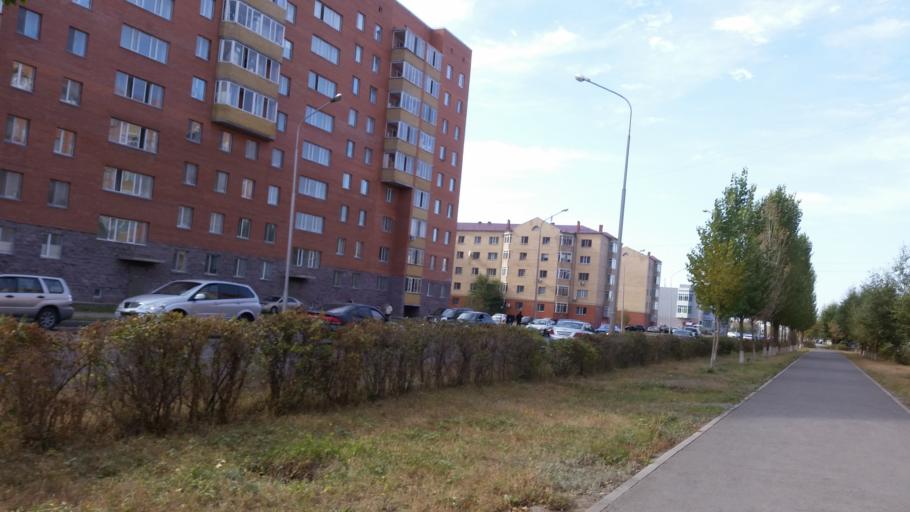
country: KZ
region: Astana Qalasy
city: Astana
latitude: 51.1602
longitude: 71.4899
